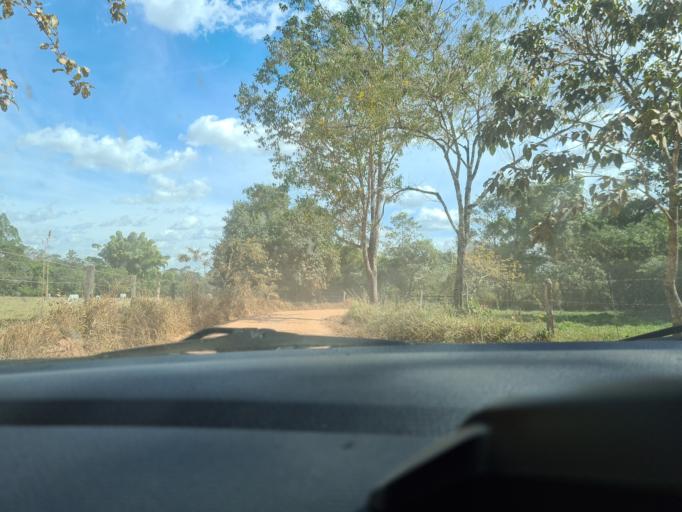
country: BR
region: Goias
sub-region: Silvania
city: Silvania
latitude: -16.5360
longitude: -48.5842
